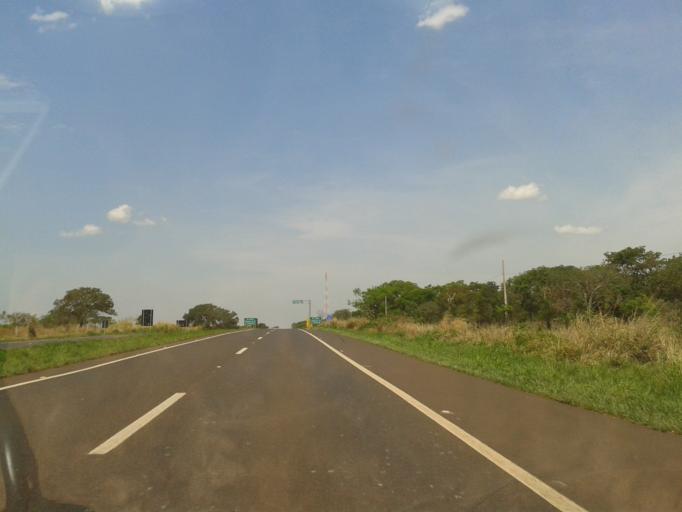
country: BR
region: Minas Gerais
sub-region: Monte Alegre De Minas
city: Monte Alegre de Minas
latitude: -18.8515
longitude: -48.7946
